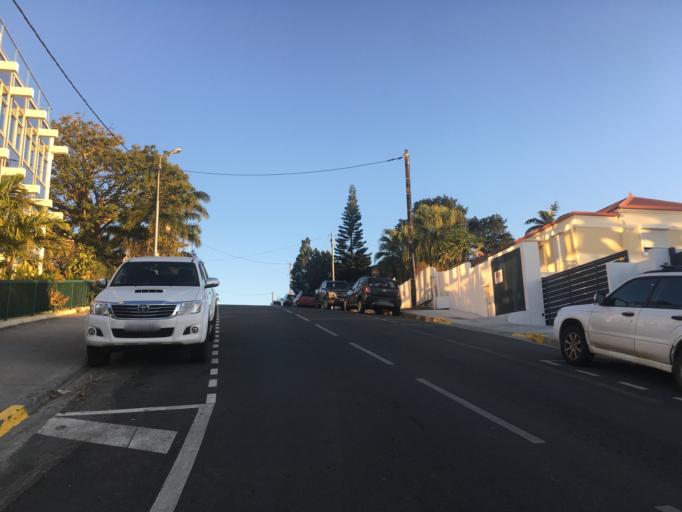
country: NC
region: South Province
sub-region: Noumea
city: Noumea
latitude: -22.2782
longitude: 166.4447
